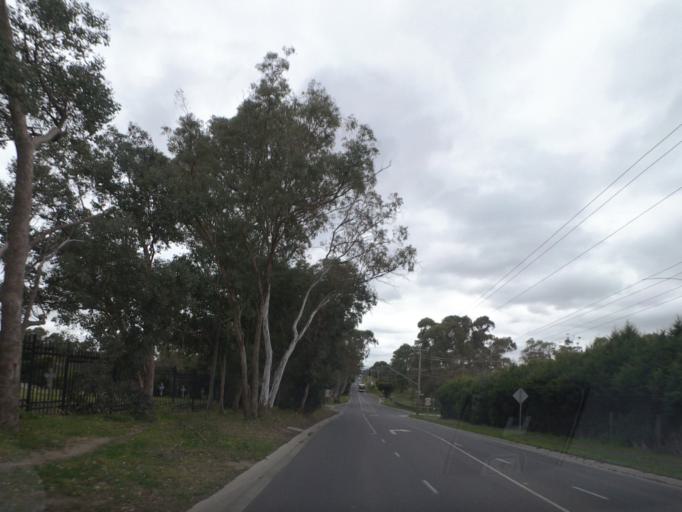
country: AU
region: Victoria
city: Plenty
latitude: -37.6354
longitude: 145.1329
